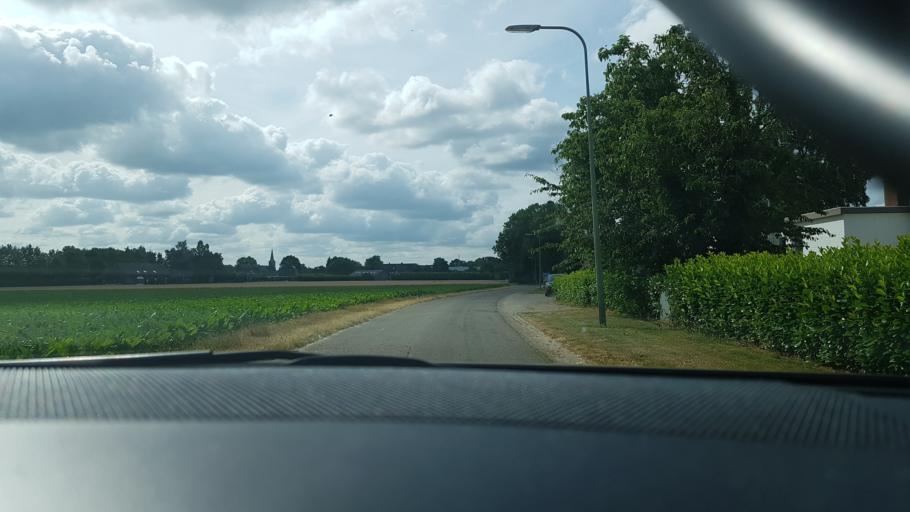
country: NL
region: Limburg
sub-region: Gemeente Beesel
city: Beesel
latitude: 51.2384
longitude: 6.0250
